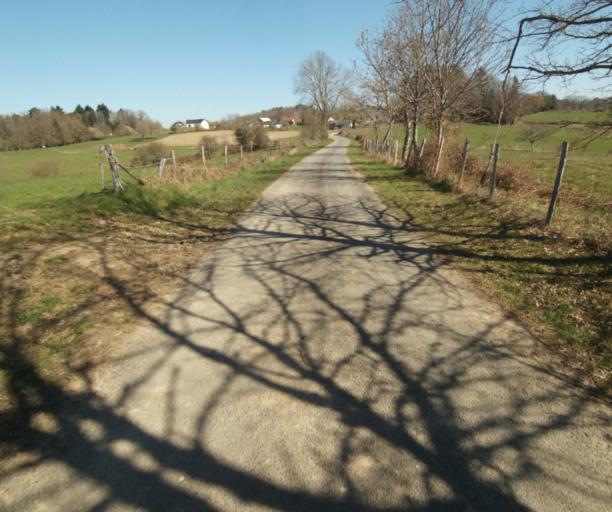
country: FR
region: Limousin
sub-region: Departement de la Correze
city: Saint-Mexant
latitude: 45.3039
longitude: 1.6001
